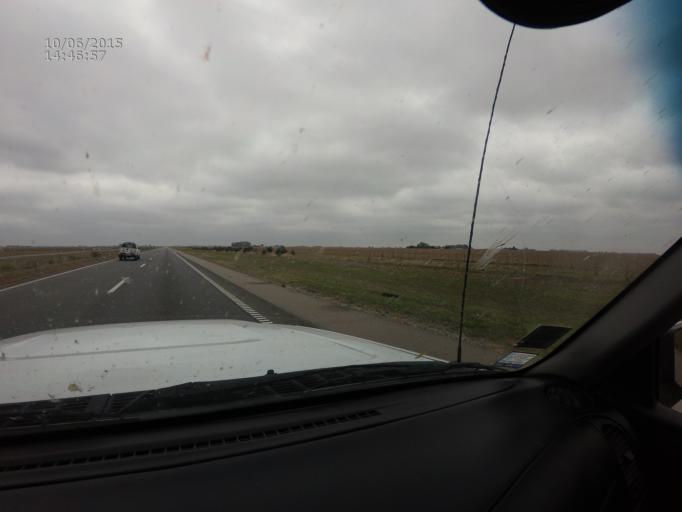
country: AR
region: Cordoba
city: Oliva
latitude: -31.9654
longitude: -63.5854
